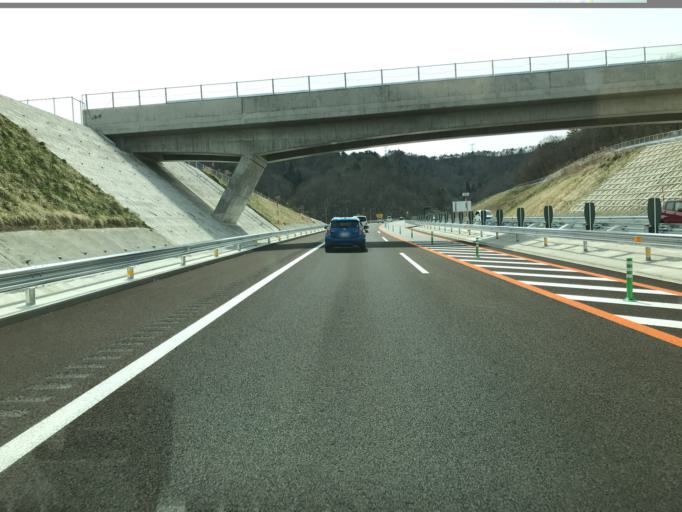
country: JP
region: Yamagata
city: Kaminoyama
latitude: 38.1187
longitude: 140.2489
